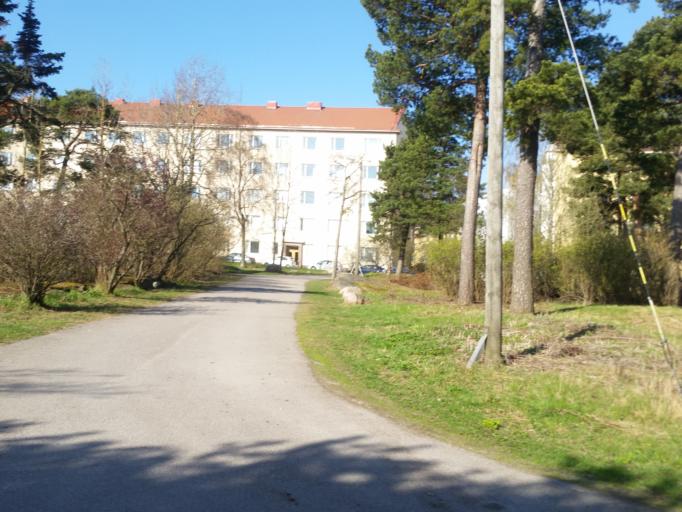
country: FI
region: Uusimaa
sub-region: Helsinki
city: Helsinki
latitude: 60.1600
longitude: 24.8939
